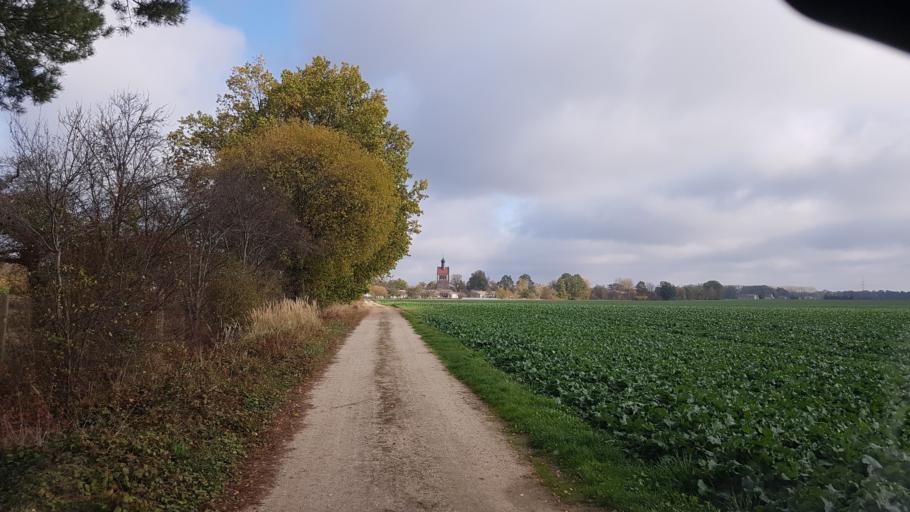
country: DE
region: Brandenburg
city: Doberlug-Kirchhain
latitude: 51.6531
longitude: 13.5274
